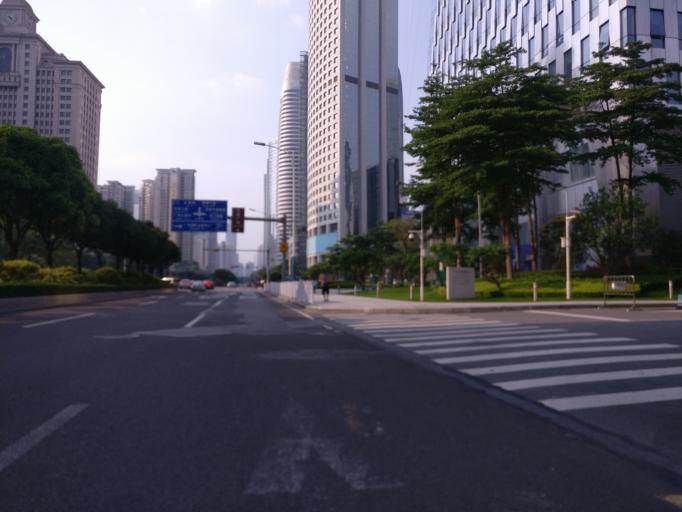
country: CN
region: Guangdong
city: Wushan
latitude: 23.1206
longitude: 113.3160
